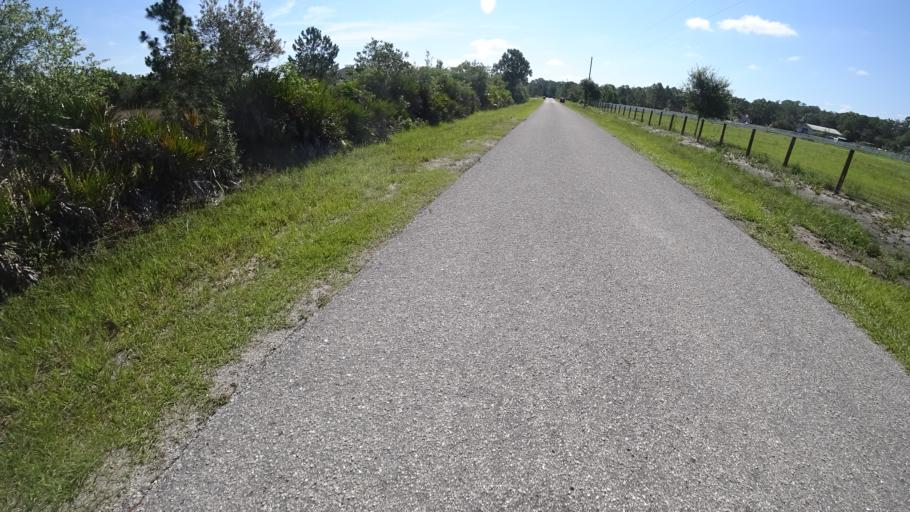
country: US
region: Florida
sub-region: Sarasota County
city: The Meadows
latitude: 27.4277
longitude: -82.3284
